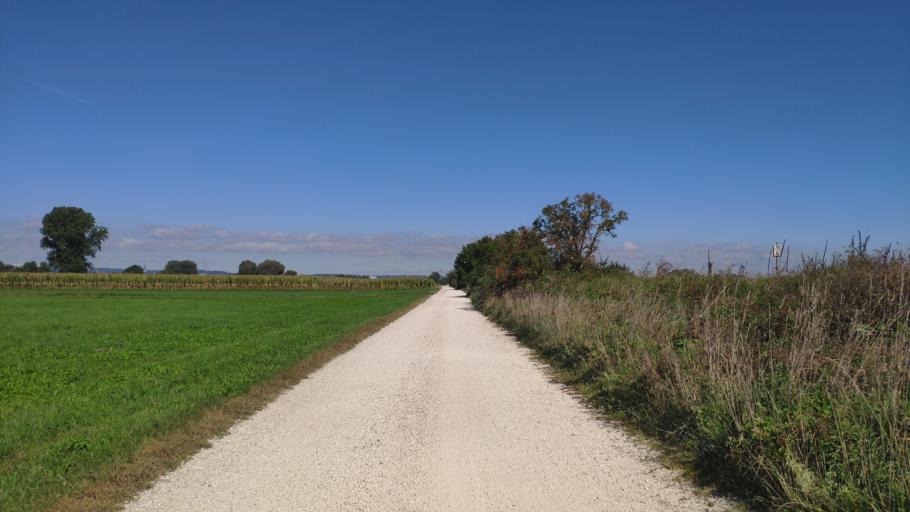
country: DE
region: Bavaria
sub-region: Swabia
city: Senden
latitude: 48.3540
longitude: 10.0363
